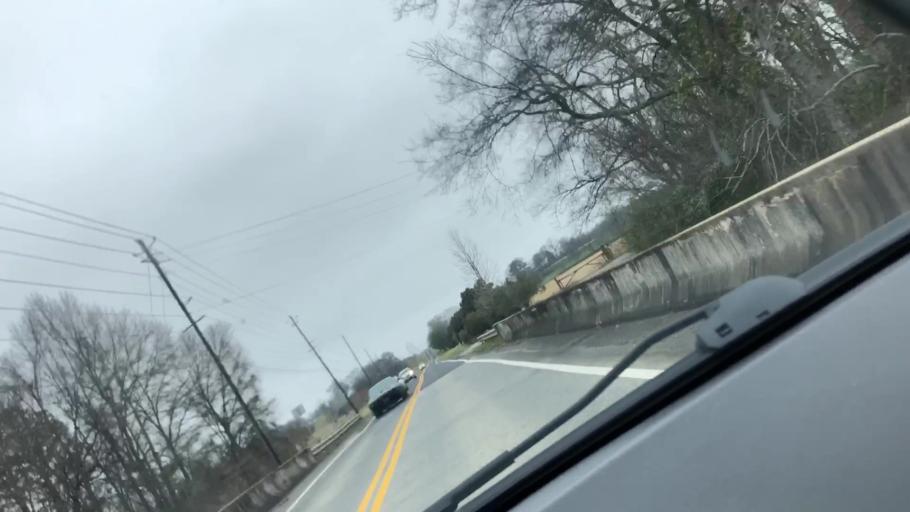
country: US
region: Georgia
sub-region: Bartow County
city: Cartersville
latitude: 34.1206
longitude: -84.8206
